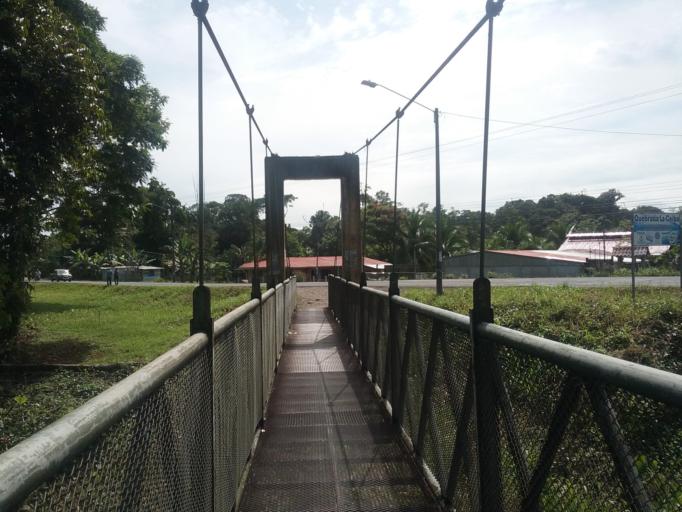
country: CR
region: Limon
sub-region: Canton de Pococi
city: Guapiles
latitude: 10.3203
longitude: -83.9097
